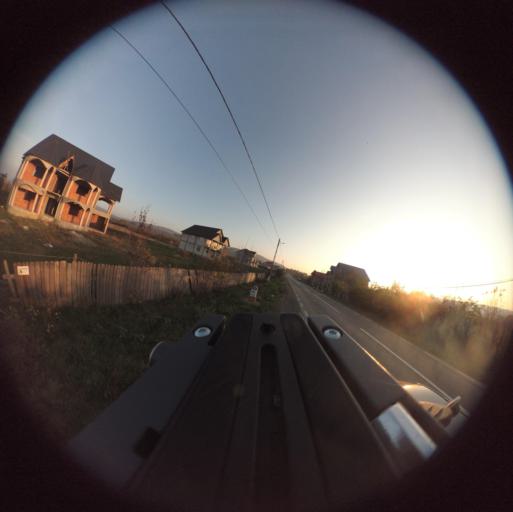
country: RO
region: Vaslui
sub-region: Comuna Bacesti
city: Bacesti
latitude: 46.8288
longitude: 27.2513
